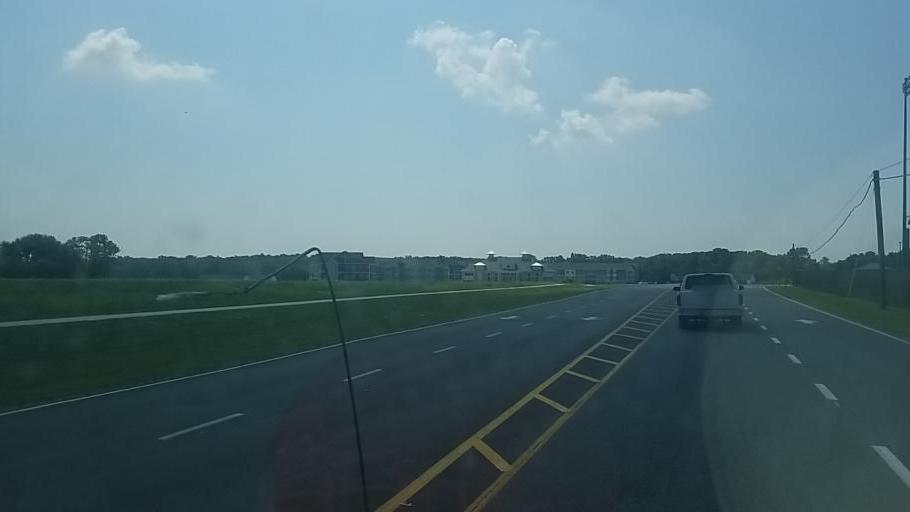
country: US
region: Maryland
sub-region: Worcester County
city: Berlin
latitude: 38.3402
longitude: -75.1884
